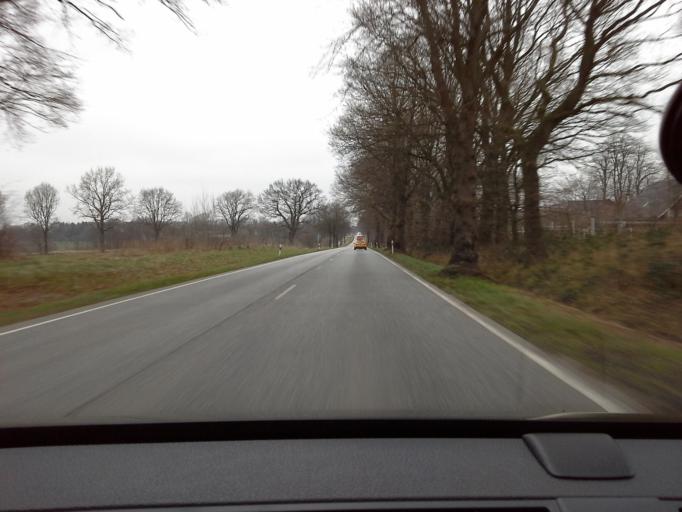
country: DE
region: Schleswig-Holstein
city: Langeln
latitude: 53.7998
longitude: 9.8778
